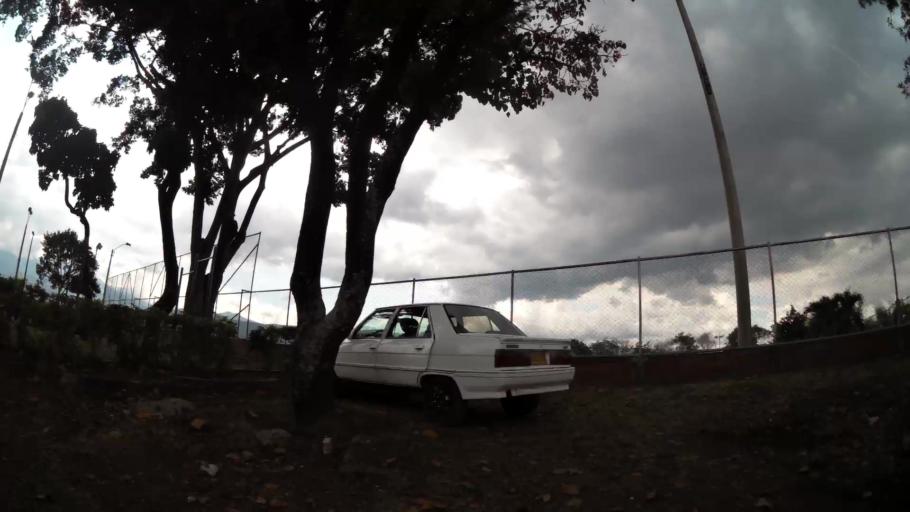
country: CO
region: Valle del Cauca
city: Cali
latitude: 3.4630
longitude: -76.4879
